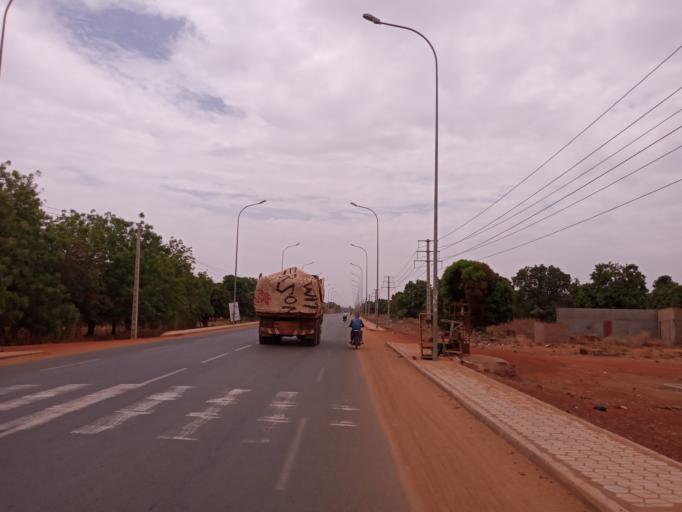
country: ML
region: Koulikoro
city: Koulikoro
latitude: 12.8494
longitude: -7.5742
